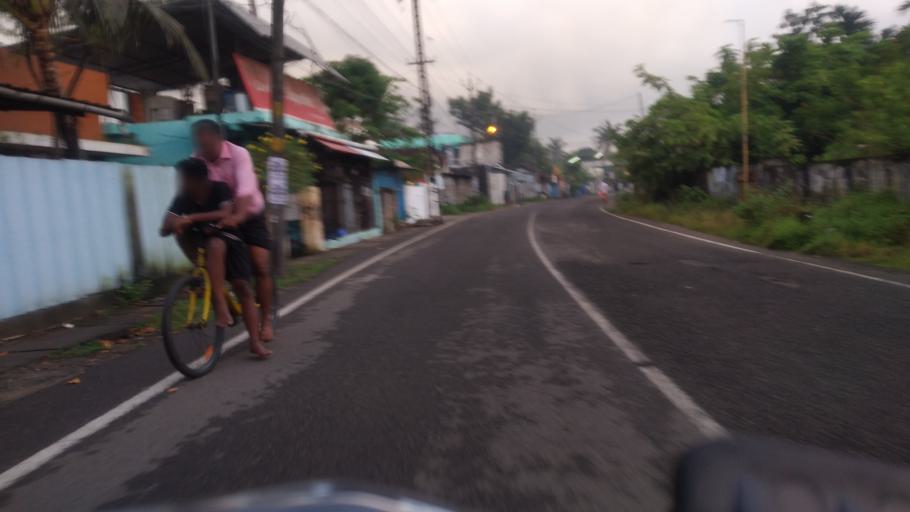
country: IN
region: Kerala
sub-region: Ernakulam
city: Cochin
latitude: 9.9780
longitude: 76.2410
